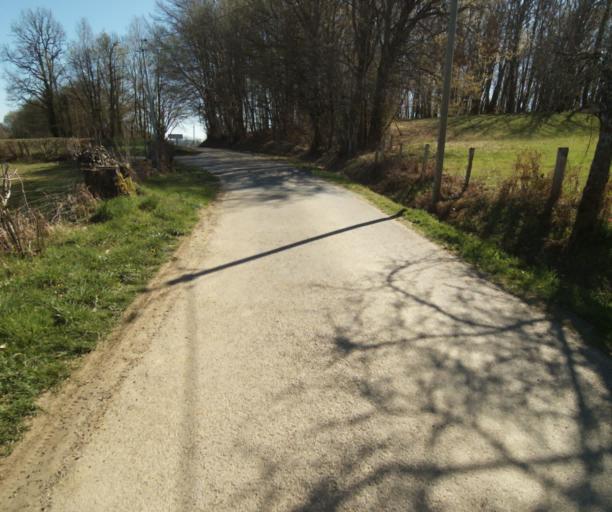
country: FR
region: Limousin
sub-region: Departement de la Correze
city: Chameyrat
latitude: 45.2525
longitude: 1.7065
